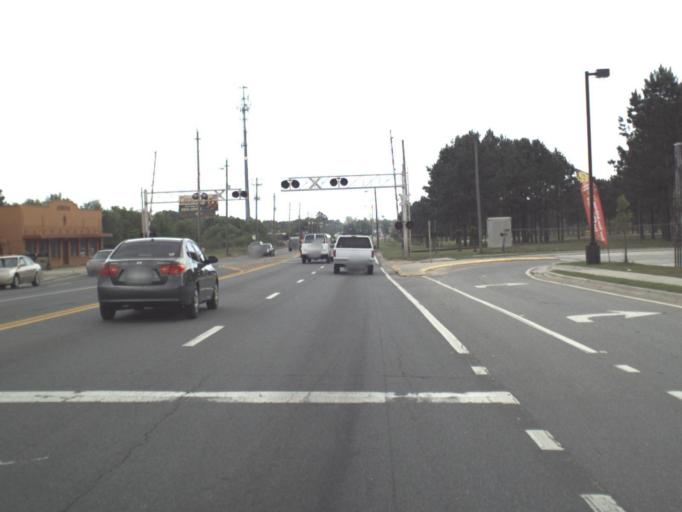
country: US
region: Florida
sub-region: Escambia County
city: Cantonment
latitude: 30.6111
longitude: -87.3202
